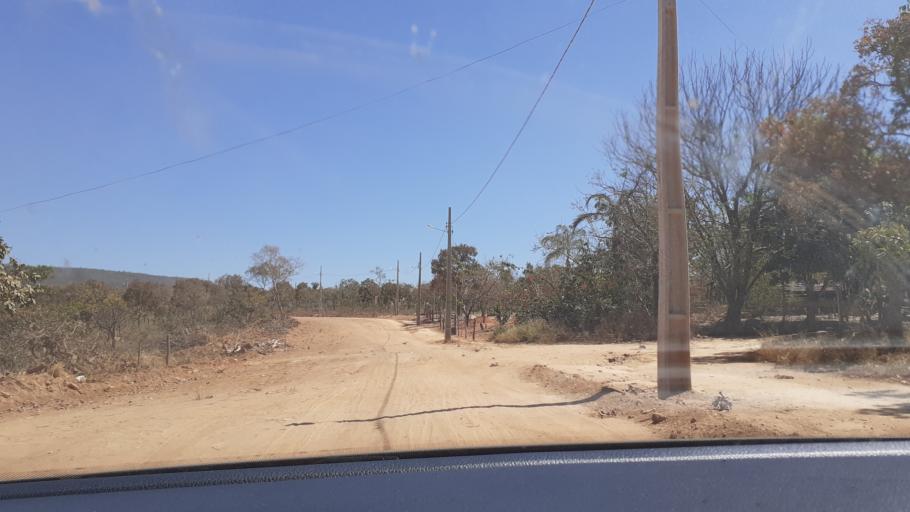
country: BR
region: Goias
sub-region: Caldas Novas
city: Caldas Novas
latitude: -17.7443
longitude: -48.6544
